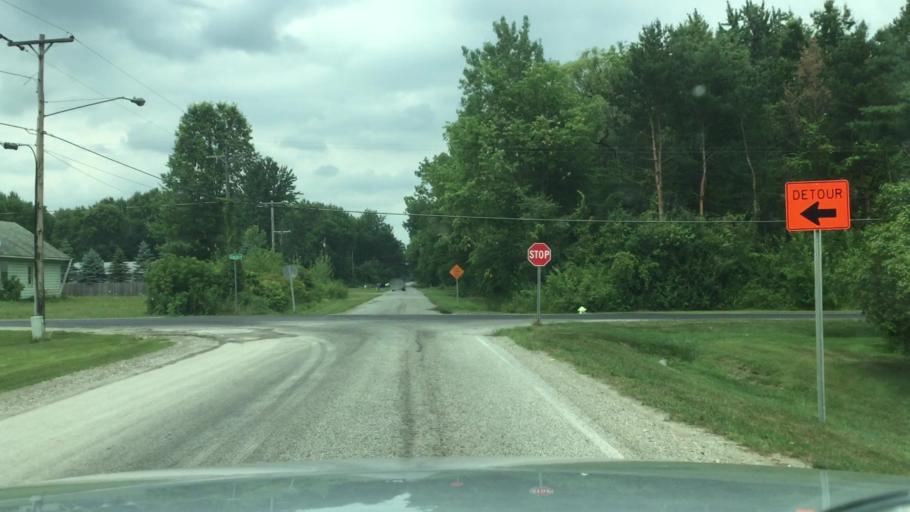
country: US
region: Michigan
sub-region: Saginaw County
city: Bridgeport
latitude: 43.3217
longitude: -83.8948
